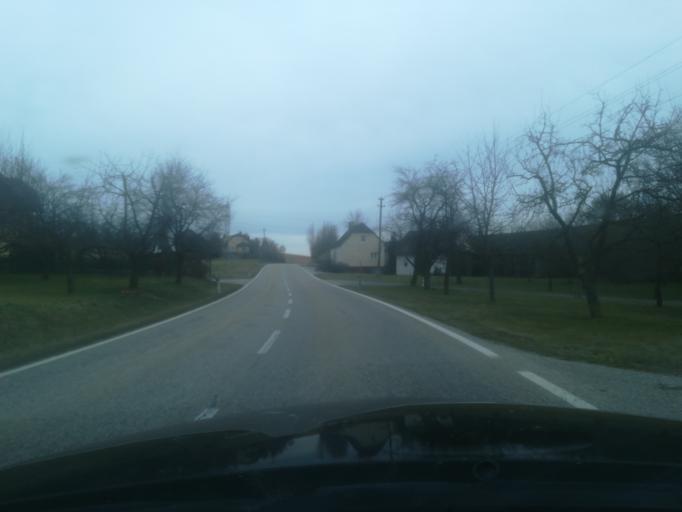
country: AT
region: Upper Austria
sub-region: Wels-Land
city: Neukirchen bei Lambach
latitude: 48.1046
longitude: 13.8259
